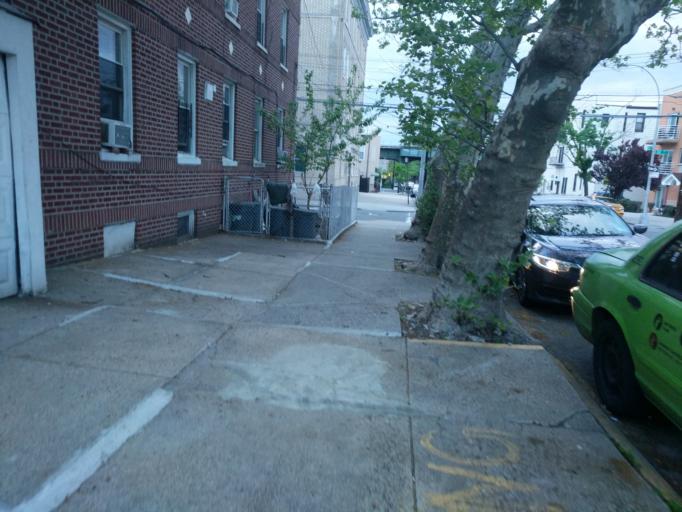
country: US
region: New York
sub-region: Queens County
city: Long Island City
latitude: 40.7728
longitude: -73.9131
